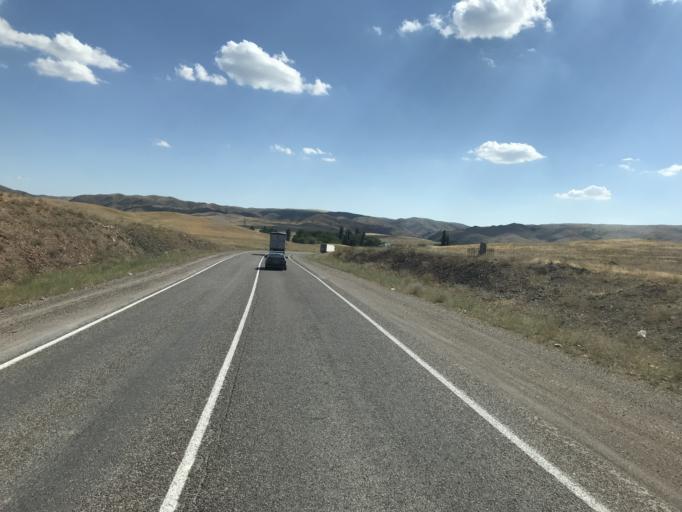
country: KZ
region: Zhambyl
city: Georgiyevka
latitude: 43.3932
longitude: 75.0656
